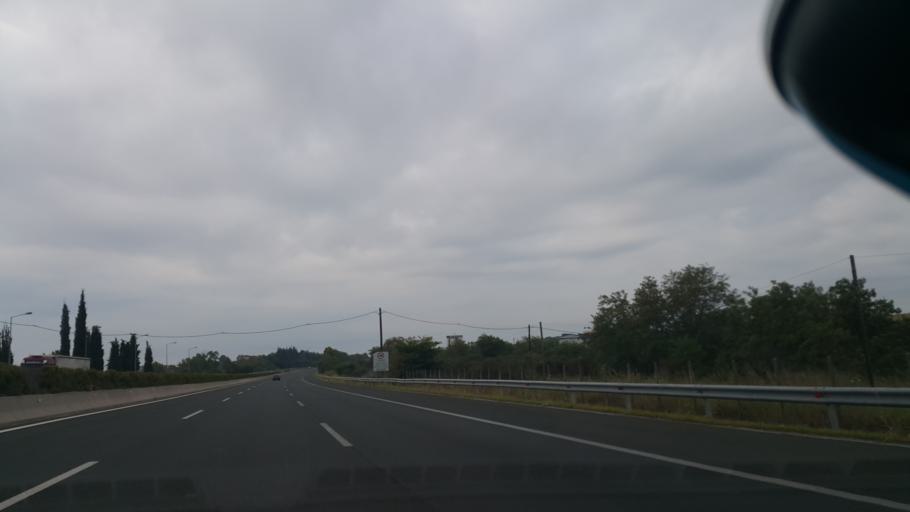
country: GR
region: Central Macedonia
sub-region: Nomos Pierias
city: Makrygialos
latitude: 40.3886
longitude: 22.6052
